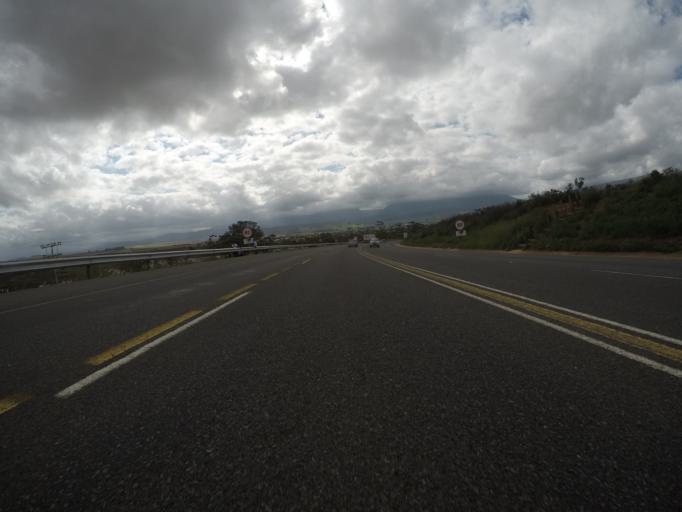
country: ZA
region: Western Cape
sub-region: Eden District Municipality
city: Riversdale
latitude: -34.1019
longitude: 21.2521
